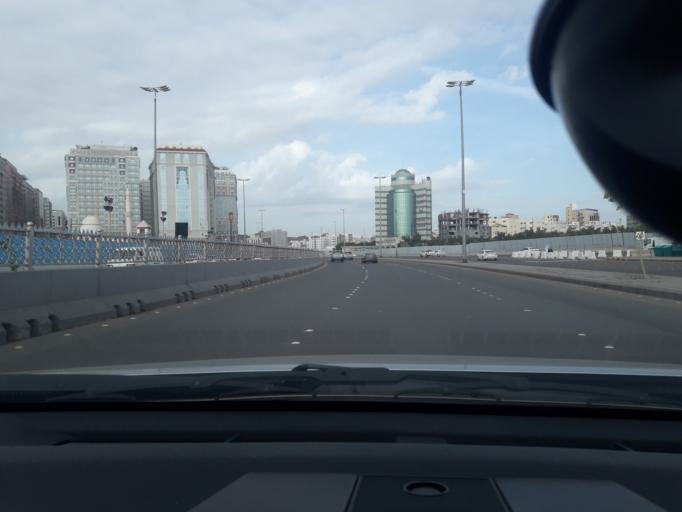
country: SA
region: Al Madinah al Munawwarah
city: Medina
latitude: 24.4729
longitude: 39.6167
